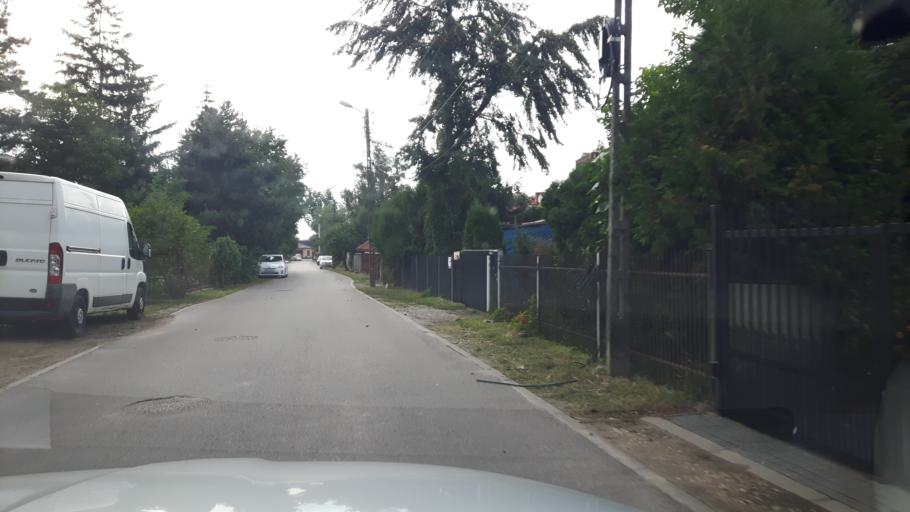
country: PL
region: Masovian Voivodeship
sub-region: Powiat wolominski
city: Marki
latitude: 52.3223
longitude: 21.1005
